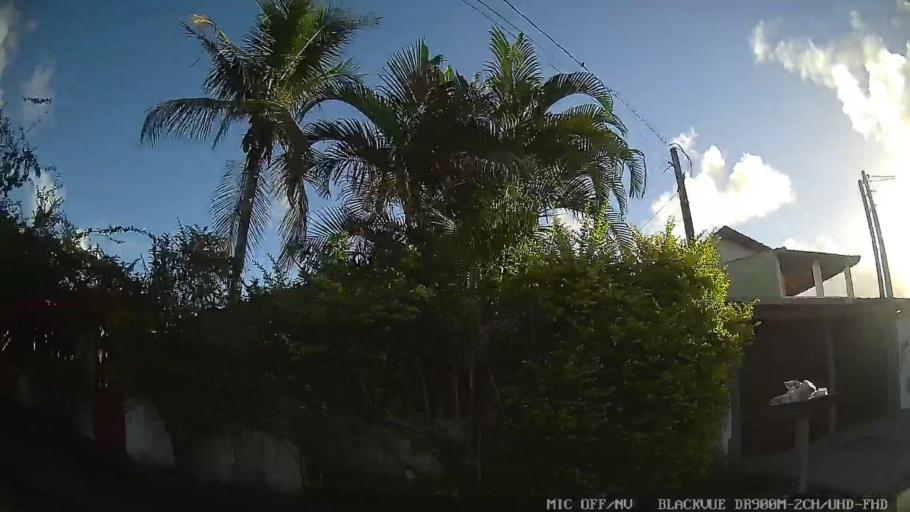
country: BR
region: Sao Paulo
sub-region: Itanhaem
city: Itanhaem
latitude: -24.1412
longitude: -46.7173
